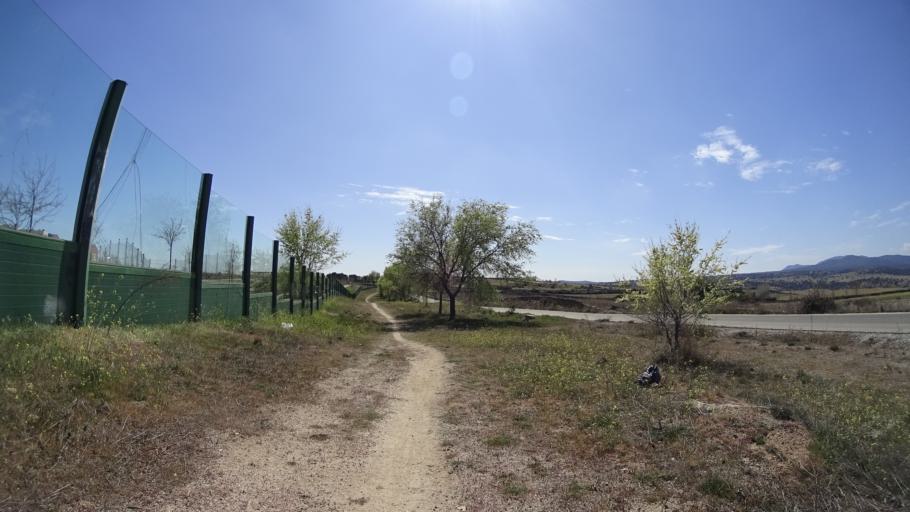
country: ES
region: Madrid
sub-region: Provincia de Madrid
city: Colmenar Viejo
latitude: 40.6508
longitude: -3.7920
